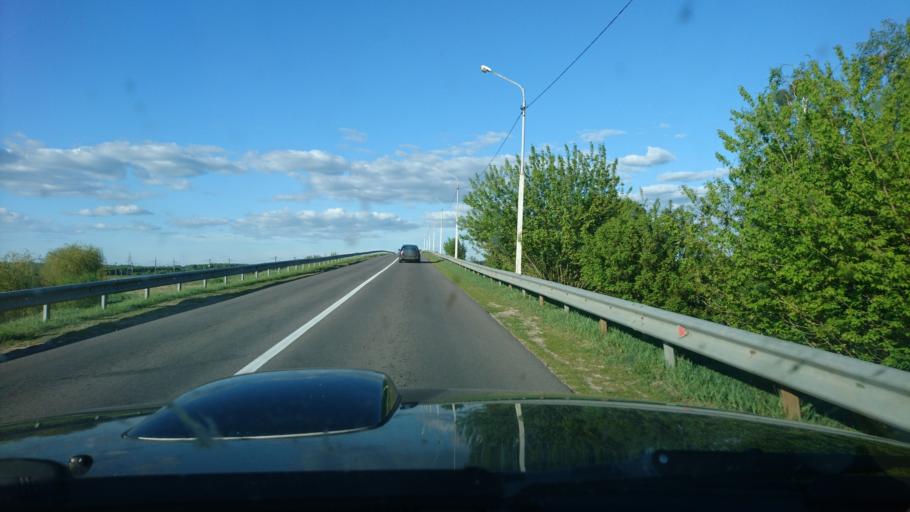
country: BY
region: Brest
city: Ivatsevichy
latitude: 52.7178
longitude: 25.3552
